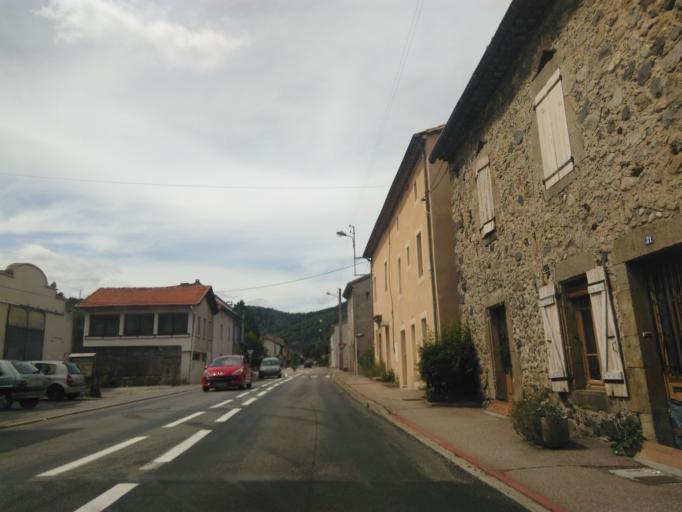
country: FR
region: Rhone-Alpes
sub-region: Departement de l'Ardeche
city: Labegude
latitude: 44.6506
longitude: 4.3222
